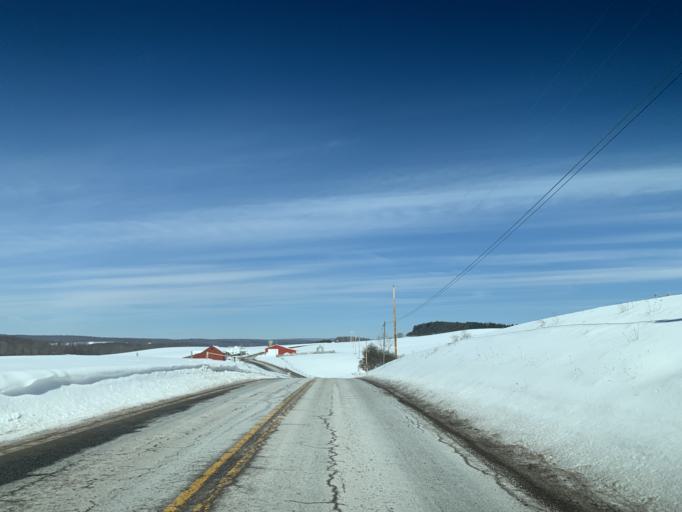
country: US
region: West Virginia
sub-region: Preston County
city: Terra Alta
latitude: 39.7141
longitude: -79.4458
